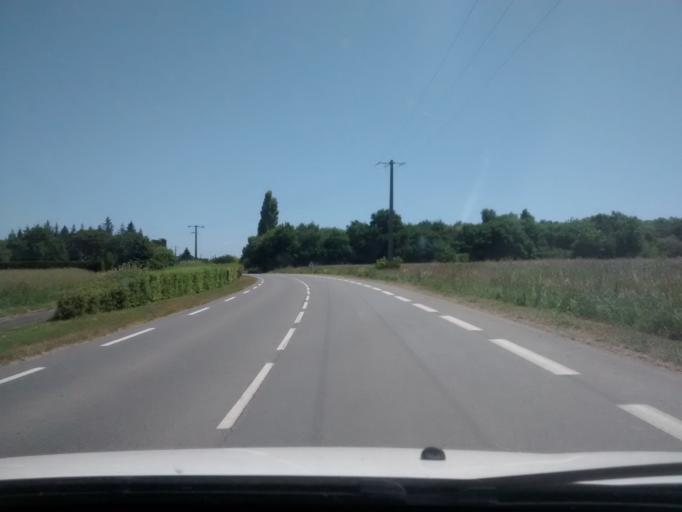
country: FR
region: Brittany
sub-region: Departement d'Ille-et-Vilaine
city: Saint-Lunaire
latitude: 48.6178
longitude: -2.1058
